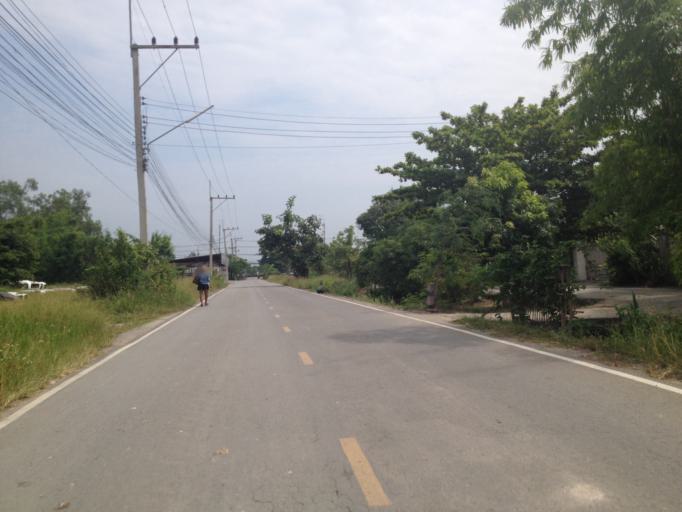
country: TH
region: Chiang Mai
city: San Pa Tong
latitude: 18.6542
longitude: 98.9035
